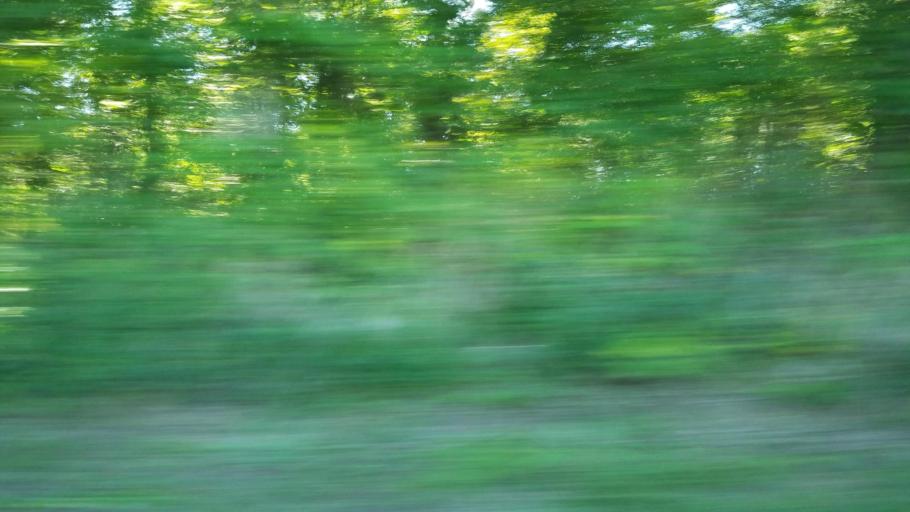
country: US
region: Illinois
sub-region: Saline County
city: Harrisburg
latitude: 37.8099
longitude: -88.6146
